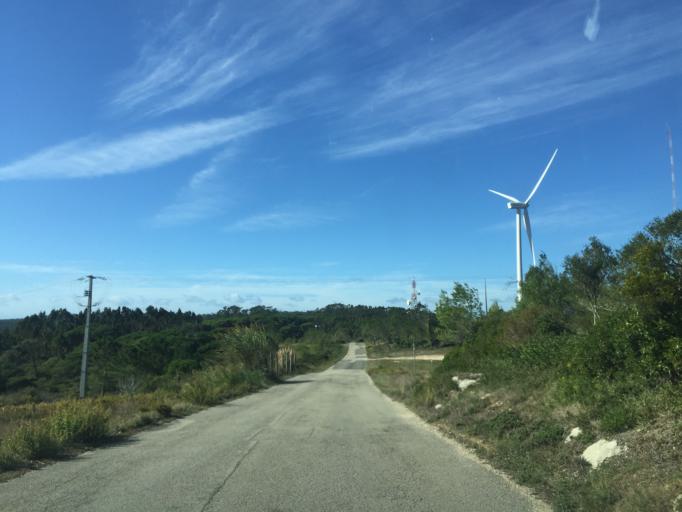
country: PT
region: Coimbra
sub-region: Figueira da Foz
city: Tavarede
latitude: 40.1958
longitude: -8.8556
